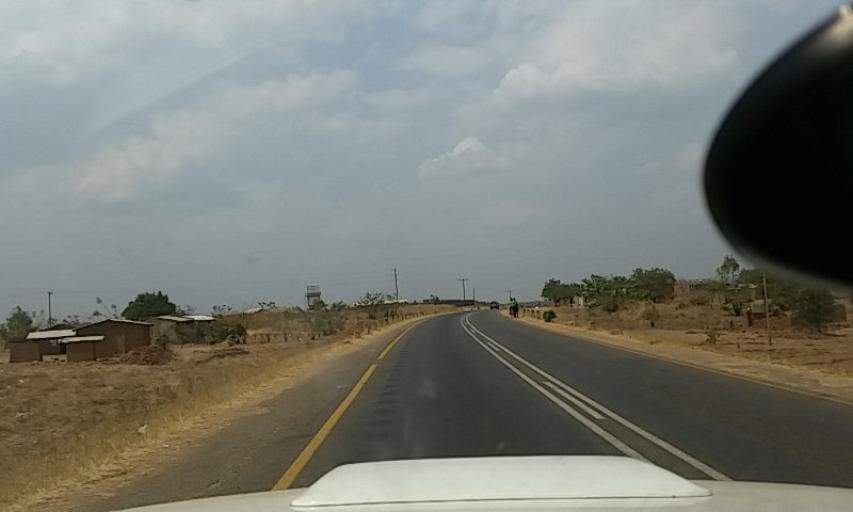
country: MW
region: Central Region
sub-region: Lilongwe District
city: Lilongwe
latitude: -13.8258
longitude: 33.8564
